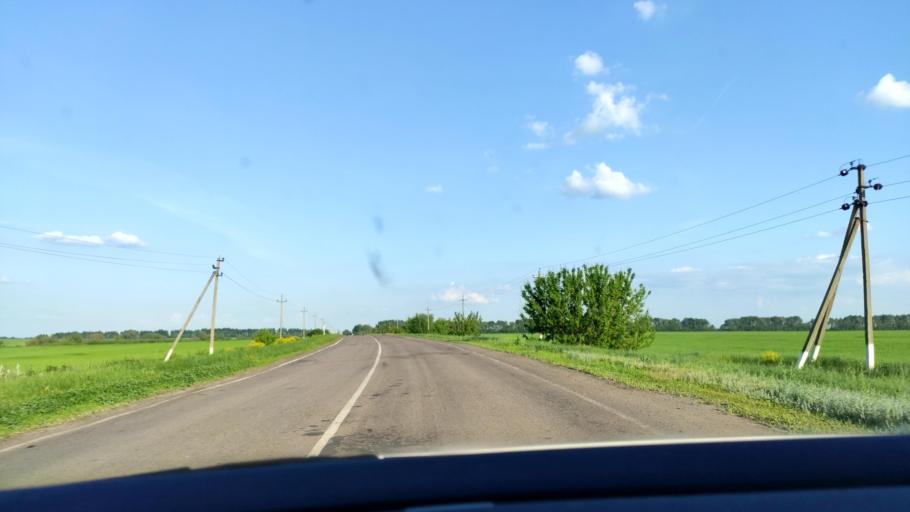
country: RU
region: Voronezj
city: Kashirskoye
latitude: 51.4965
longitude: 39.8360
